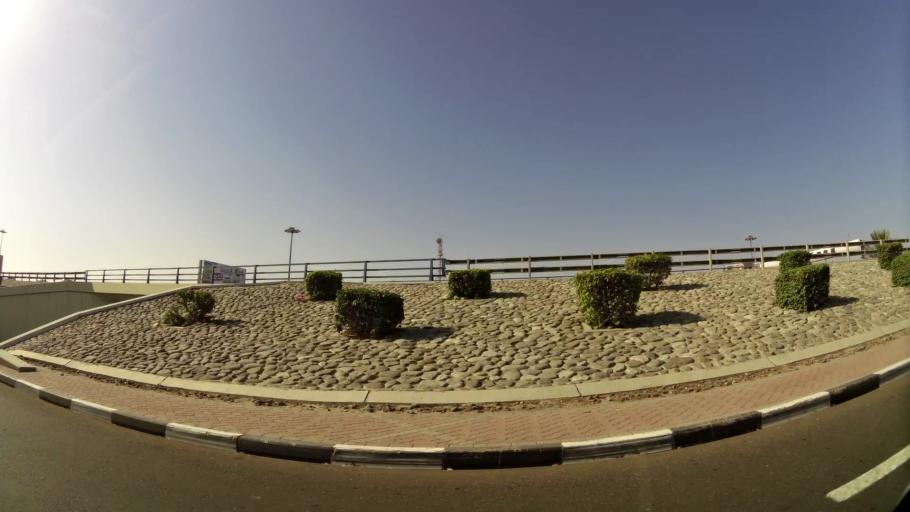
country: AE
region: Ash Shariqah
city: Sharjah
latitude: 25.2489
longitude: 55.3160
